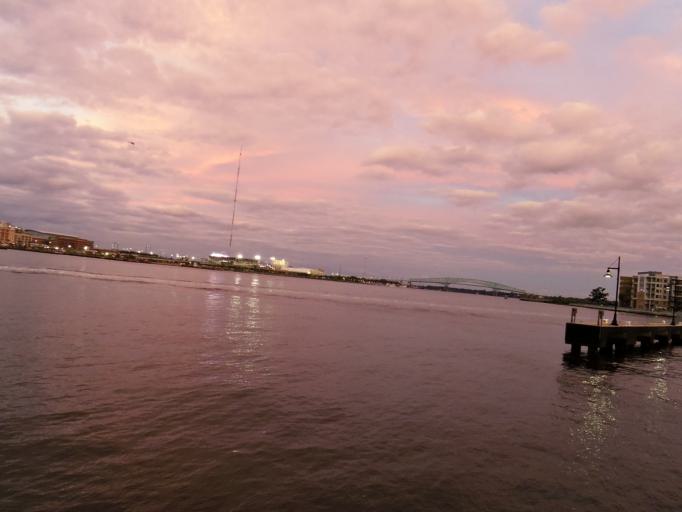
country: US
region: Florida
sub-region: Duval County
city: Jacksonville
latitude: 30.3191
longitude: -81.6544
